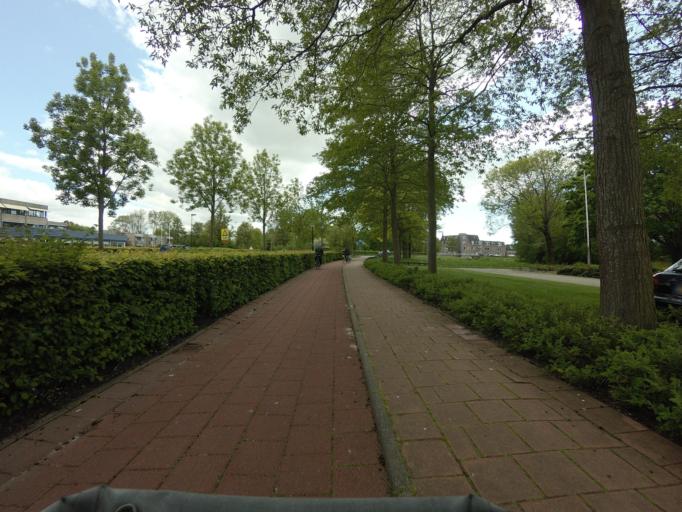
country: NL
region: Friesland
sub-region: Sudwest Fryslan
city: Bolsward
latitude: 53.0670
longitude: 5.5295
